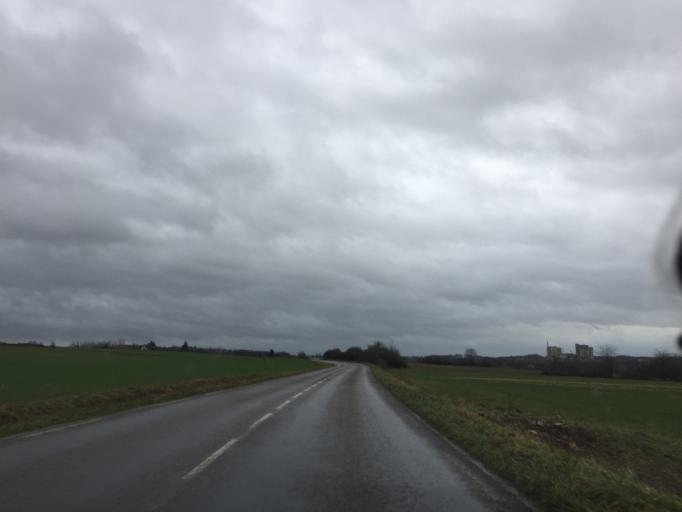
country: FR
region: Franche-Comte
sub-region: Departement du Jura
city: Dole
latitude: 47.1525
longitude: 5.5662
